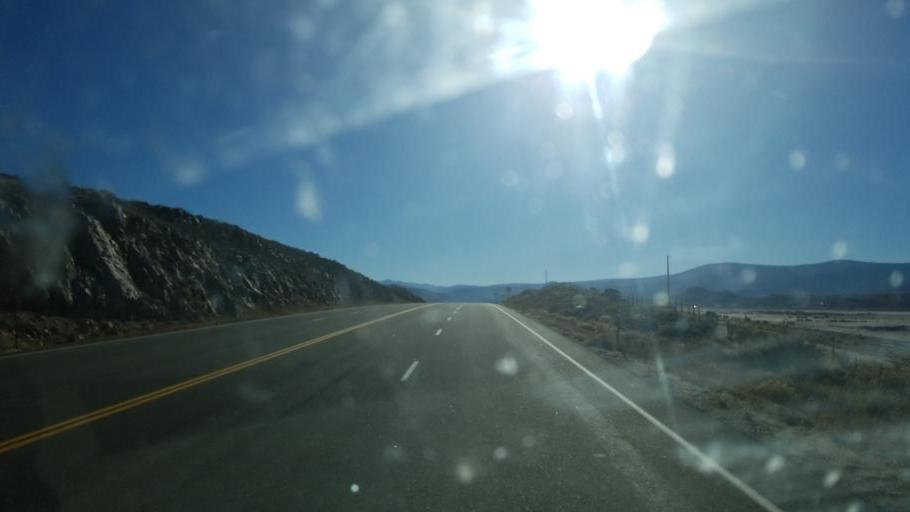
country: US
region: Colorado
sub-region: Gunnison County
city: Gunnison
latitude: 38.4596
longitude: -106.6252
